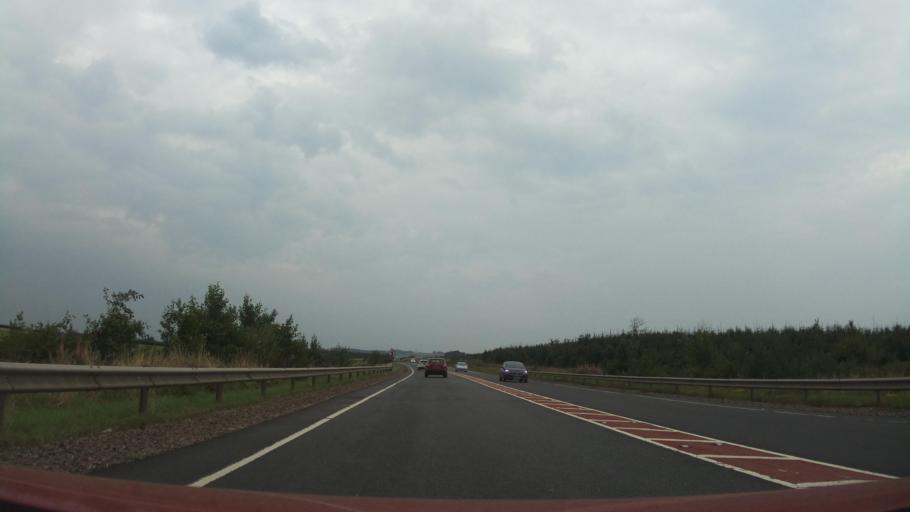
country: GB
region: Scotland
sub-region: Dumfries and Galloway
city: Lockerbie
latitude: 55.0175
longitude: -3.3612
